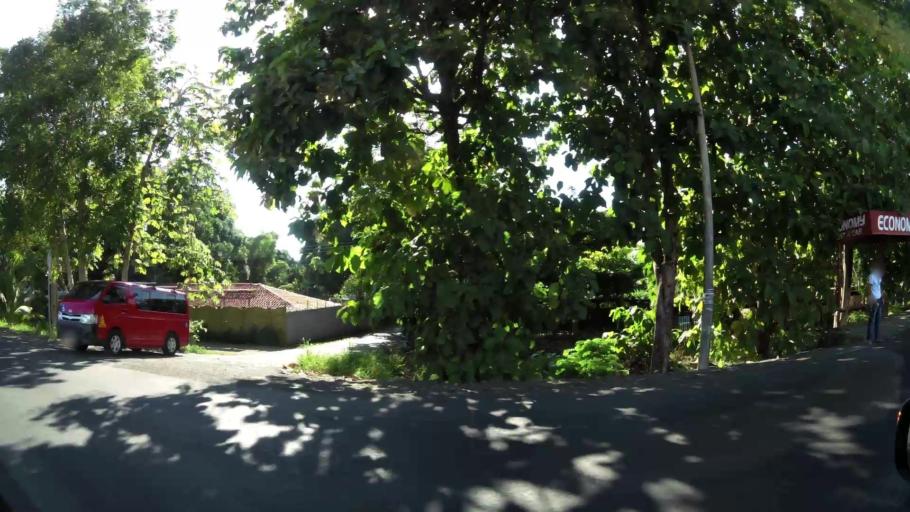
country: CR
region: Puntarenas
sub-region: Canton de Garabito
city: Jaco
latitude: 9.6112
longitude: -84.6167
